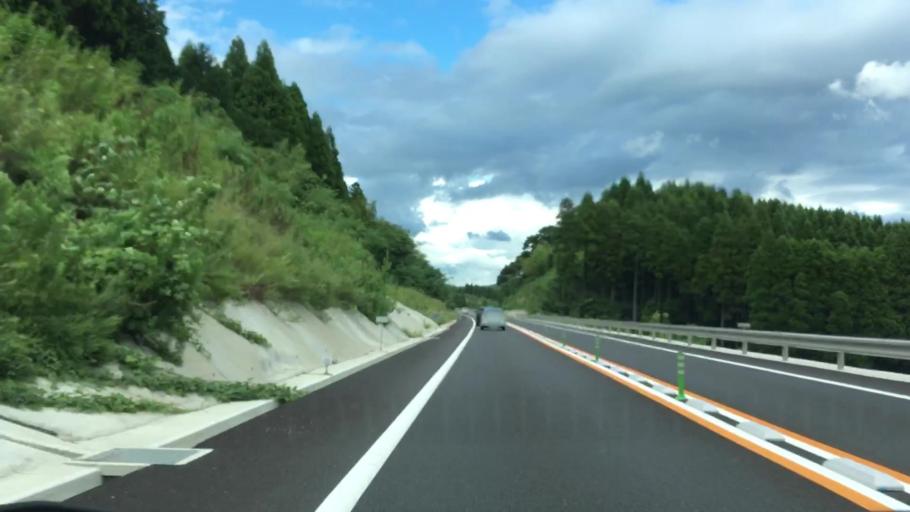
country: JP
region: Saga Prefecture
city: Imaricho-ko
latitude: 33.3163
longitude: 129.9218
